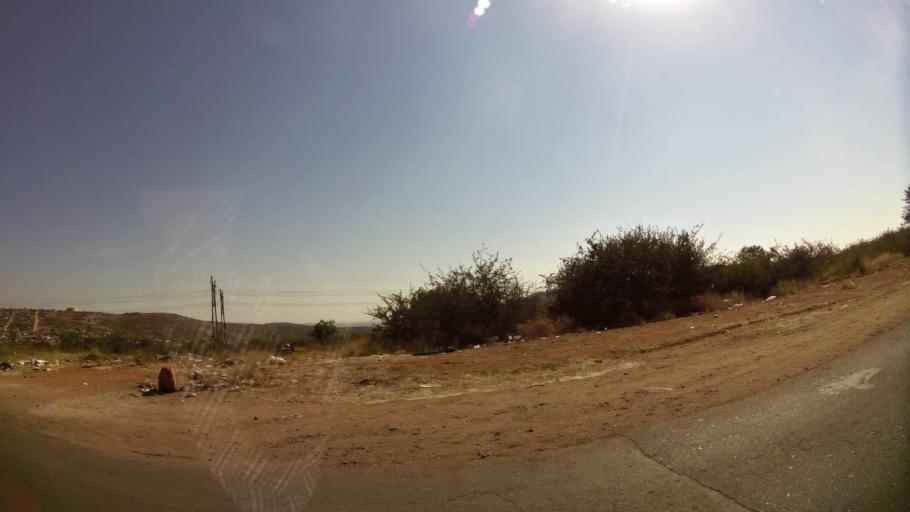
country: ZA
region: Gauteng
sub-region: City of Tshwane Metropolitan Municipality
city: Mabopane
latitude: -25.5403
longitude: 28.0805
